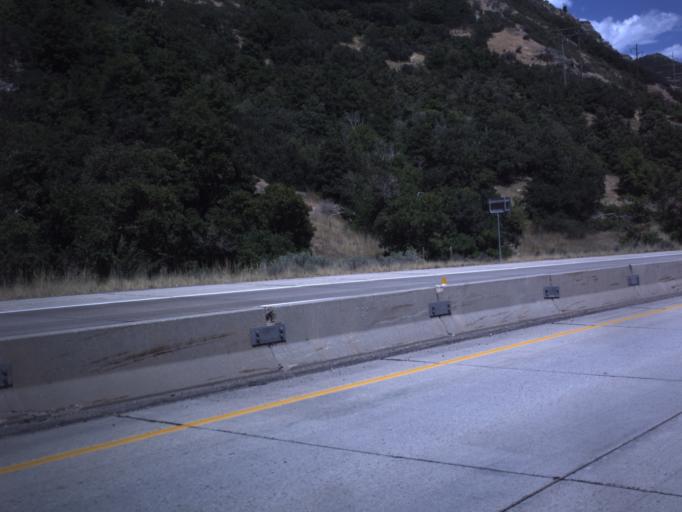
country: US
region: Utah
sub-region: Utah County
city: Orem
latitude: 40.3509
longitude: -111.5871
